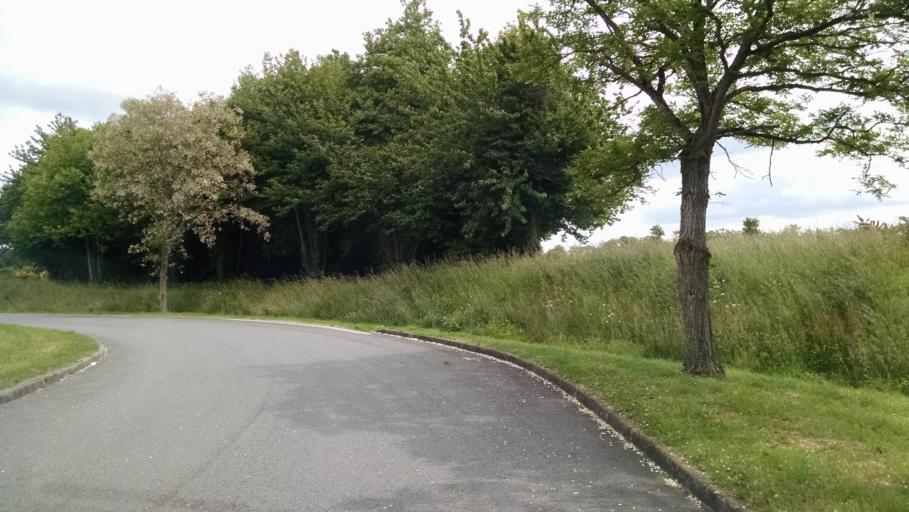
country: FR
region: Brittany
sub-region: Departement du Morbihan
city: Pluneret
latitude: 47.6606
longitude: -2.9715
